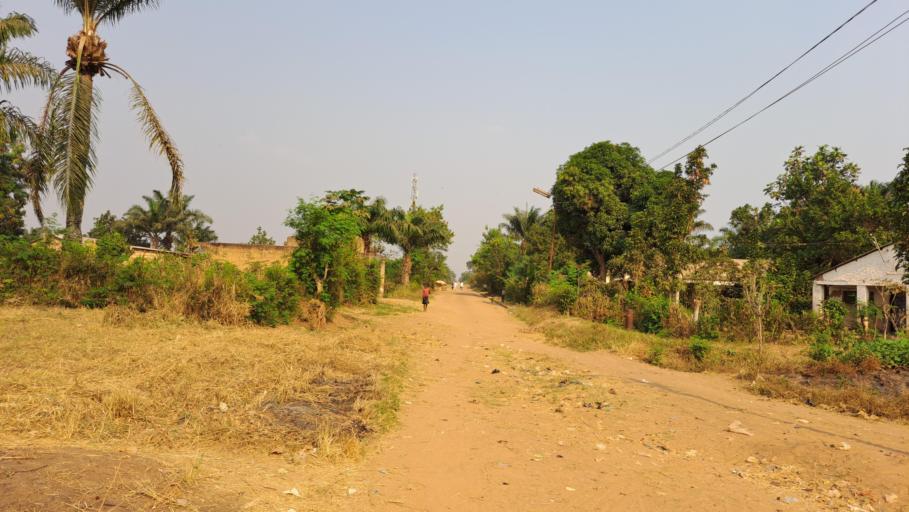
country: CD
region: Kasai-Oriental
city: Mbuji-Mayi
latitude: -6.1379
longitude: 23.5902
